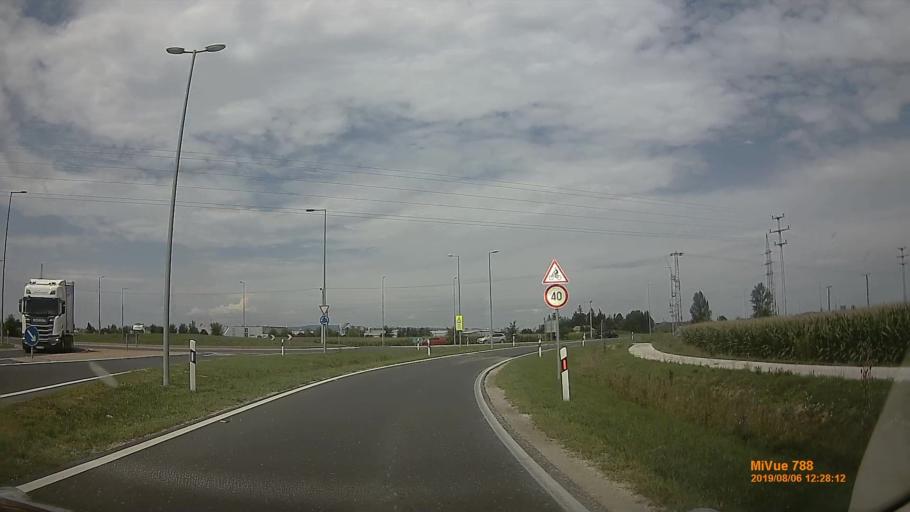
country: HU
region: Vas
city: Szombathely
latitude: 47.2203
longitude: 16.6585
